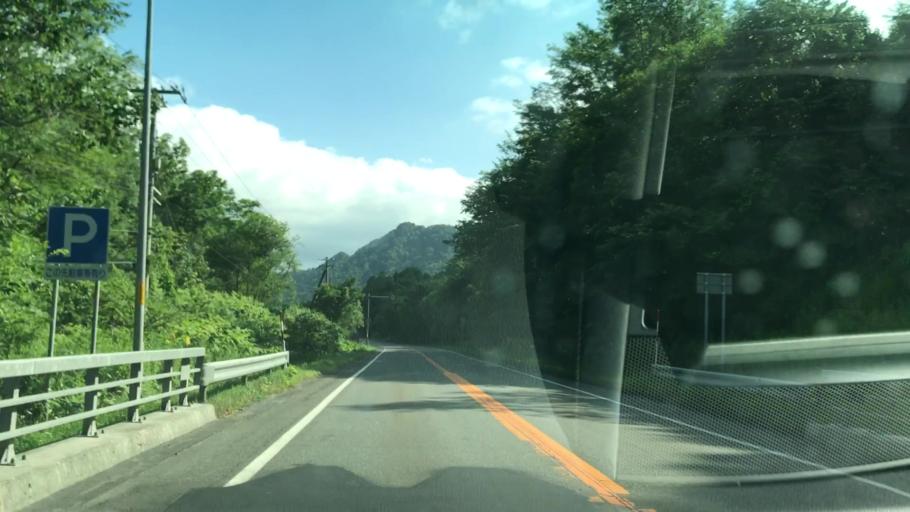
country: JP
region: Hokkaido
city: Shizunai-furukawacho
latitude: 42.8399
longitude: 142.4159
